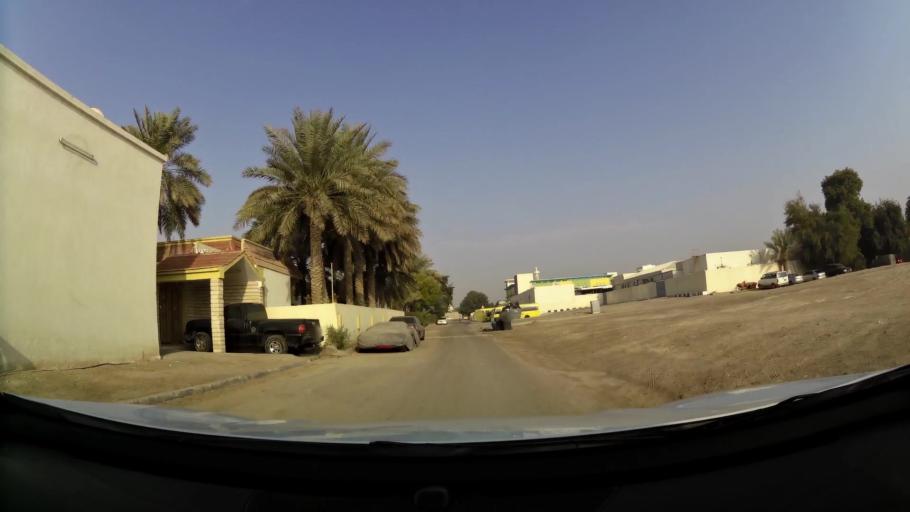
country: AE
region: Abu Dhabi
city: Abu Dhabi
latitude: 24.2848
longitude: 54.6397
